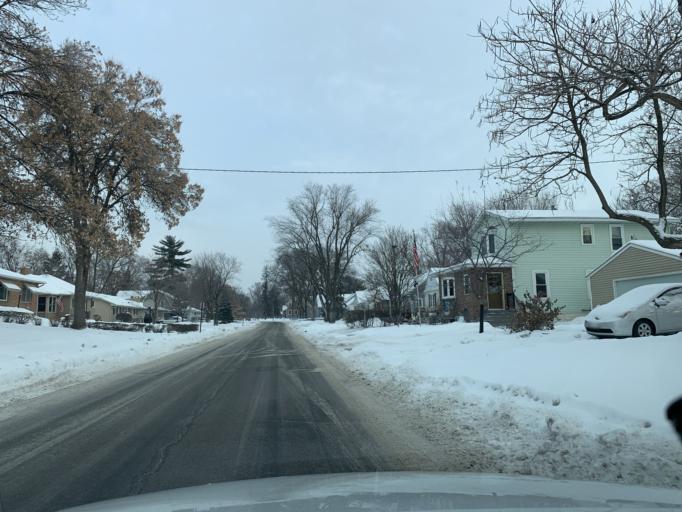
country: US
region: Minnesota
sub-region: Hennepin County
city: Saint Louis Park
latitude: 44.9227
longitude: -93.3529
